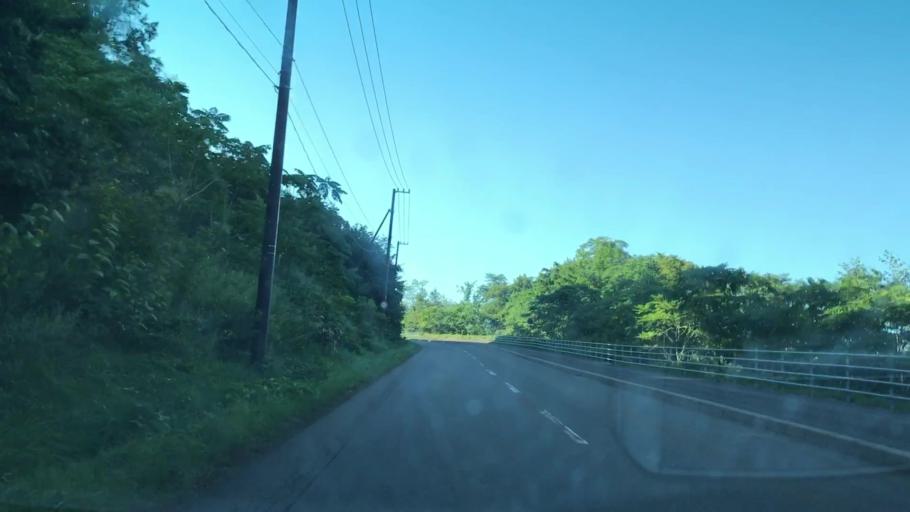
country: JP
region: Hokkaido
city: Date
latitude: 42.5653
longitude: 140.8061
